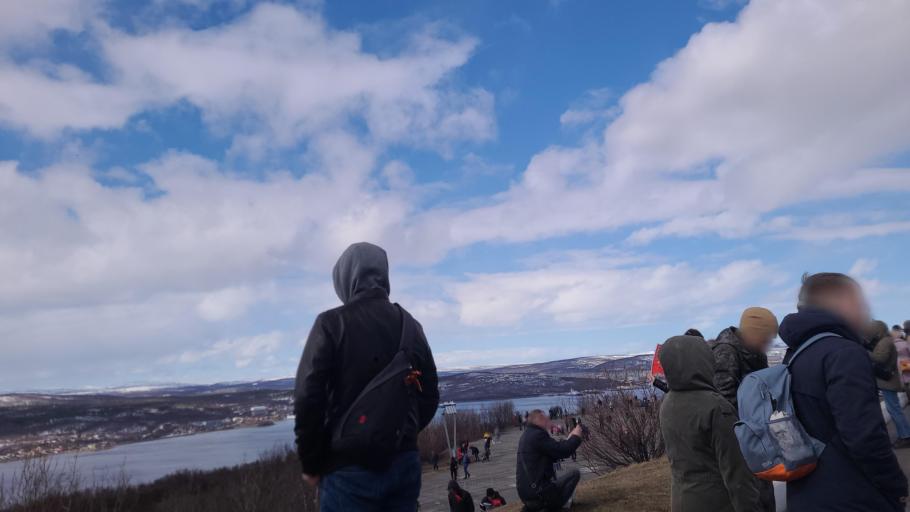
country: RU
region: Murmansk
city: Murmansk
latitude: 68.9925
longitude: 33.0708
